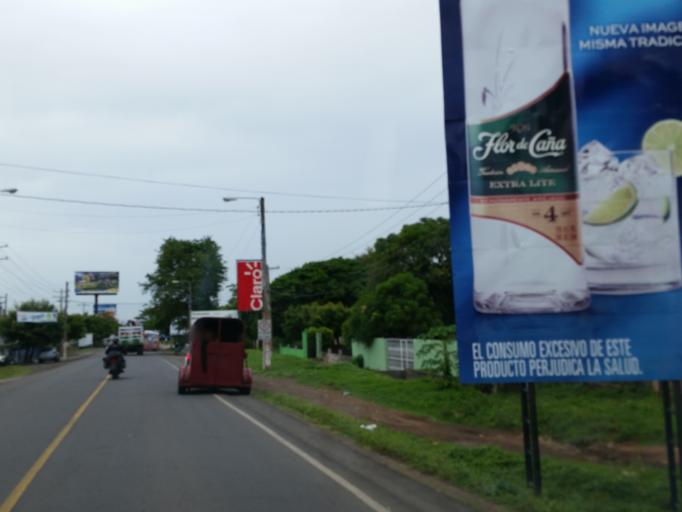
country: NI
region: Granada
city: Granada
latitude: 11.9361
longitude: -85.9676
